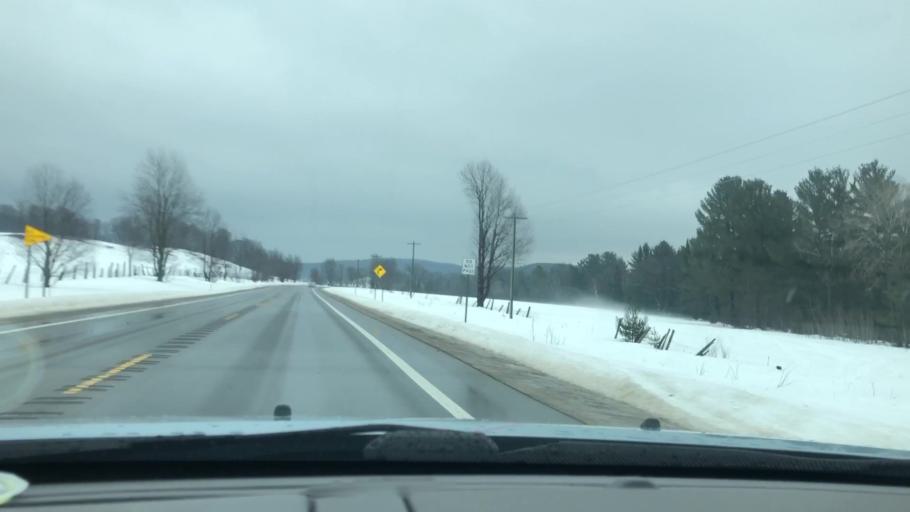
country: US
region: Michigan
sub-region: Charlevoix County
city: Boyne City
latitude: 45.0943
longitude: -84.9575
